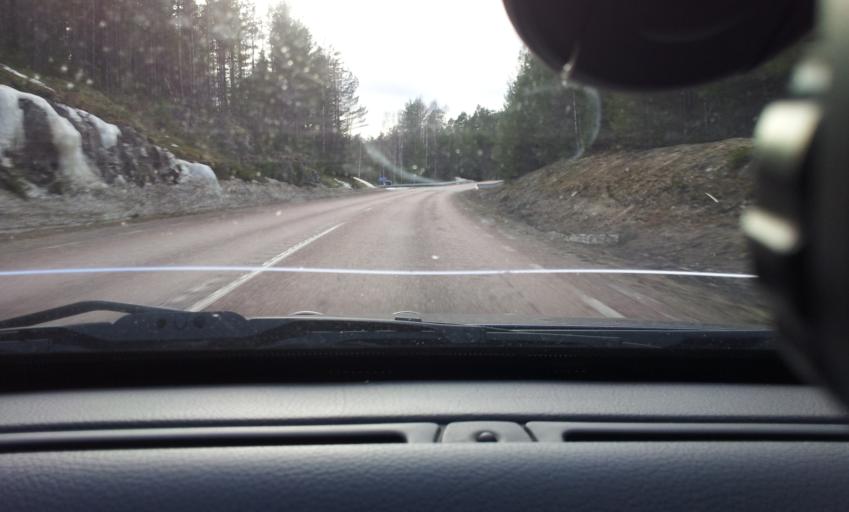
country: SE
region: Gaevleborg
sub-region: Ljusdals Kommun
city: Farila
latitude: 61.8878
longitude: 15.6811
